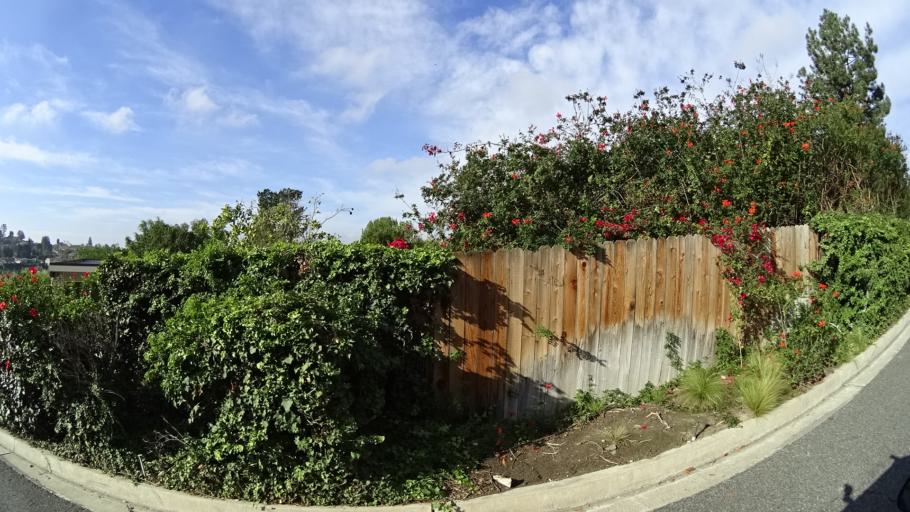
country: US
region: California
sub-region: Orange County
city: North Tustin
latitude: 33.7743
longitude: -117.7734
